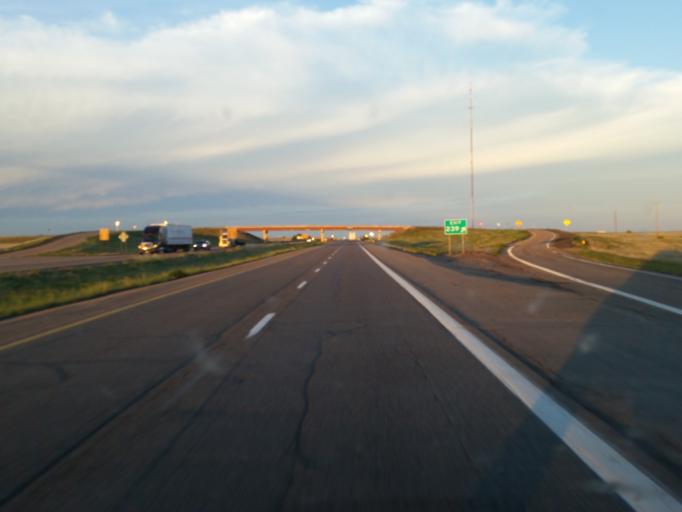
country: US
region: New Mexico
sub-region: San Miguel County
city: Las Vegas
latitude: 34.9915
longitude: -105.2972
